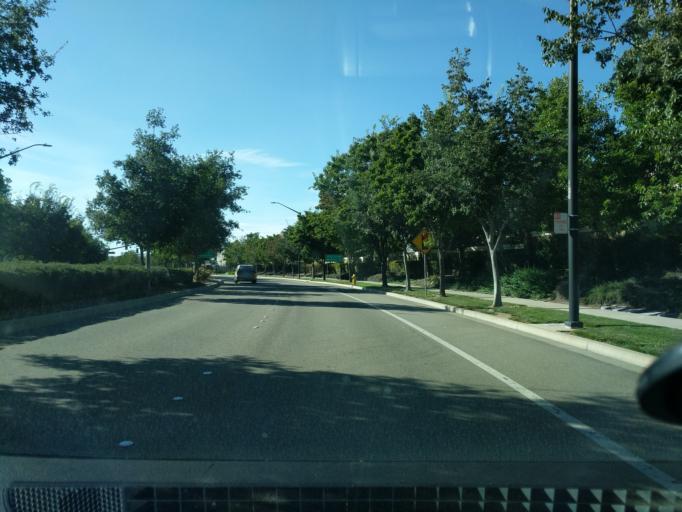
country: US
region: California
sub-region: Contra Costa County
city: Blackhawk
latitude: 37.7600
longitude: -121.8867
